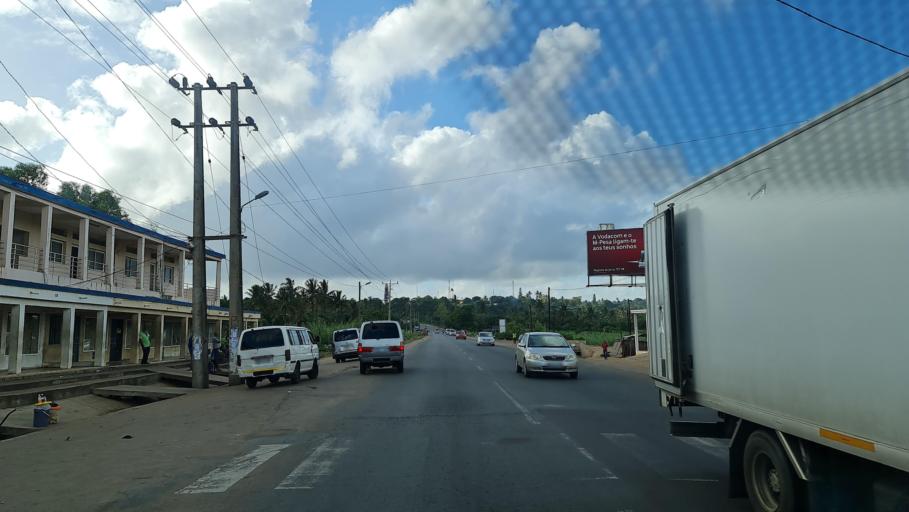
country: MZ
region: Gaza
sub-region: Xai-Xai District
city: Xai-Xai
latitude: -25.0518
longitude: 33.6480
